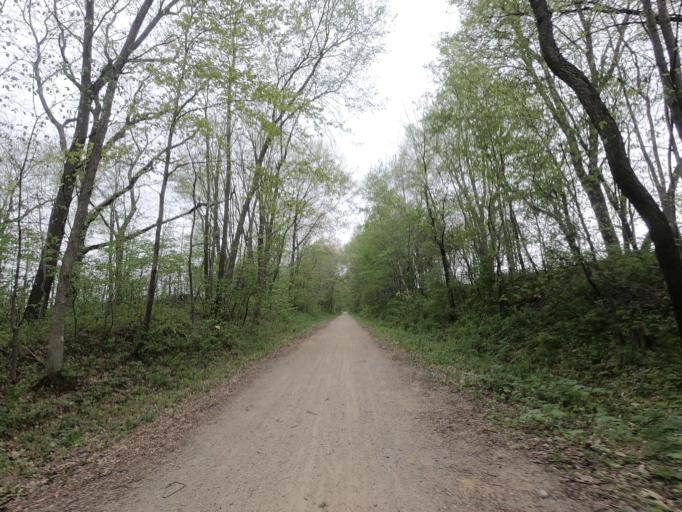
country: US
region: Wisconsin
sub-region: Jefferson County
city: Jefferson
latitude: 43.0415
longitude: -88.8429
